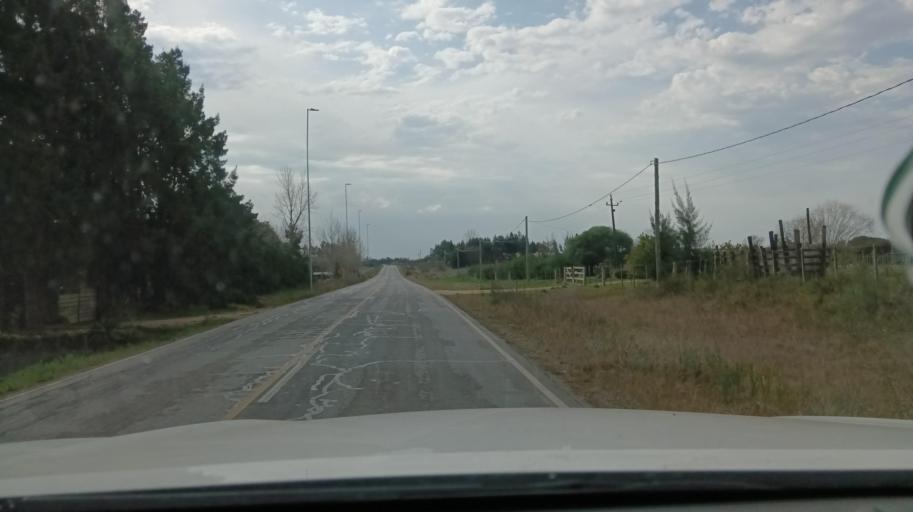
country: UY
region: Canelones
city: Sauce
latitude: -34.6620
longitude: -56.1096
